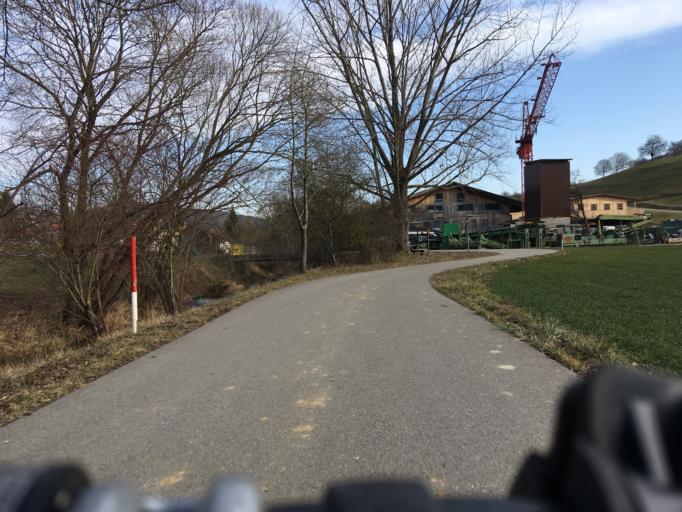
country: CH
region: Schaffhausen
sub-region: Bezirk Reiat
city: Stetten
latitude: 47.7746
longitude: 8.6719
